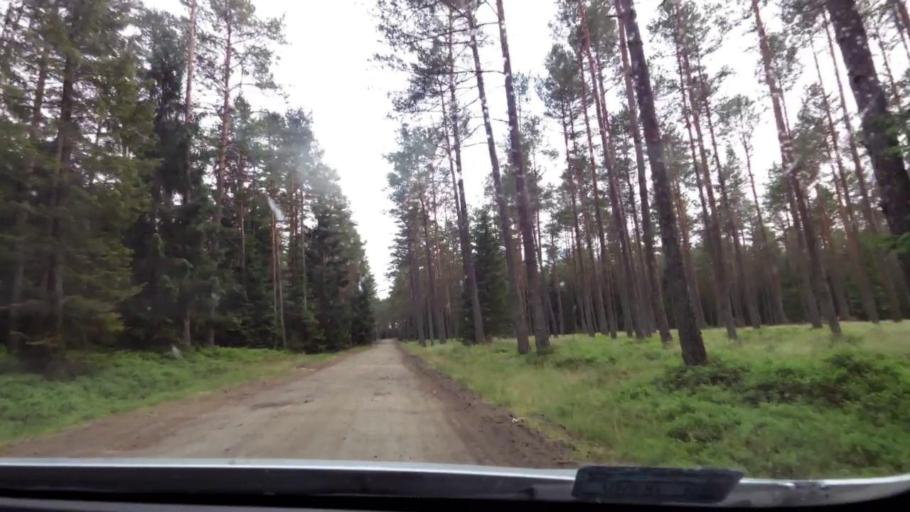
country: PL
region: Pomeranian Voivodeship
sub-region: Powiat bytowski
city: Trzebielino
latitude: 54.2125
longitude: 17.0044
